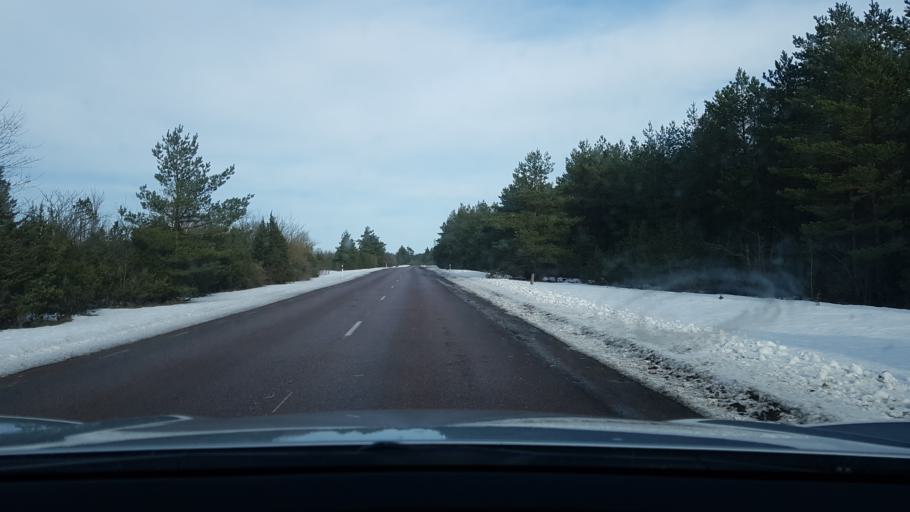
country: EE
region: Saare
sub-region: Kuressaare linn
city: Kuressaare
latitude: 58.3336
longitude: 22.5652
